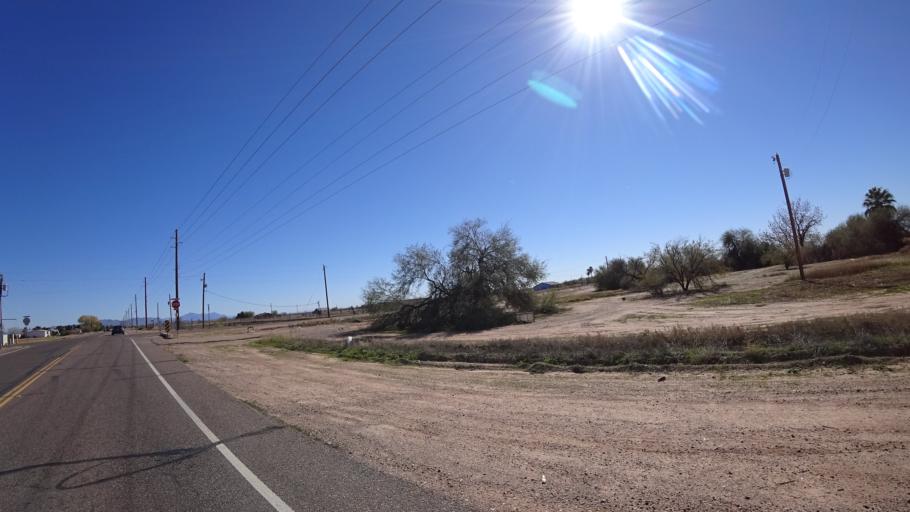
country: US
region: Arizona
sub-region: Maricopa County
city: Scottsdale
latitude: 33.4950
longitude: -111.8746
